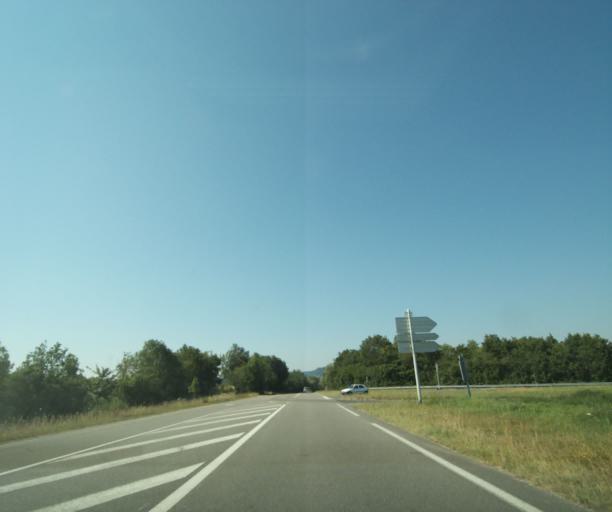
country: FR
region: Lorraine
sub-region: Departement de Meurthe-et-Moselle
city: Ecrouves
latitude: 48.6486
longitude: 5.8694
